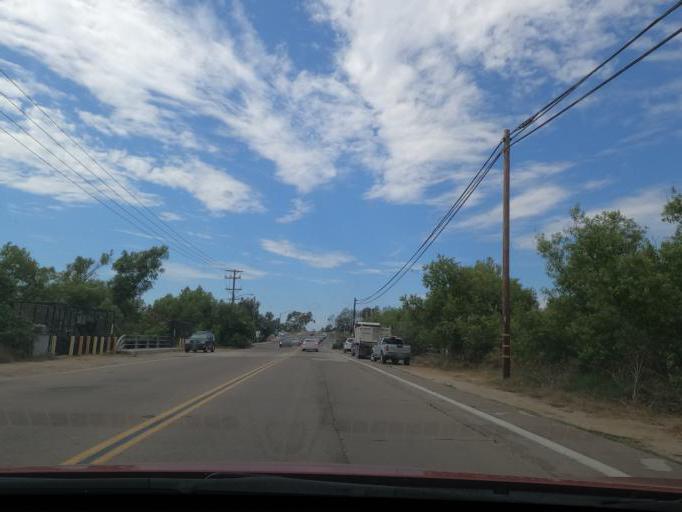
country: US
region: California
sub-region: San Diego County
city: Imperial Beach
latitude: 32.5559
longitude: -117.0624
